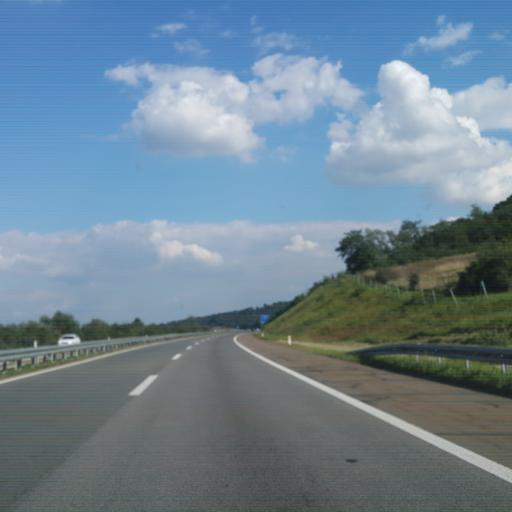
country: RS
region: Central Serbia
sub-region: Belgrade
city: Grocka
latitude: 44.5795
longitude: 20.7806
